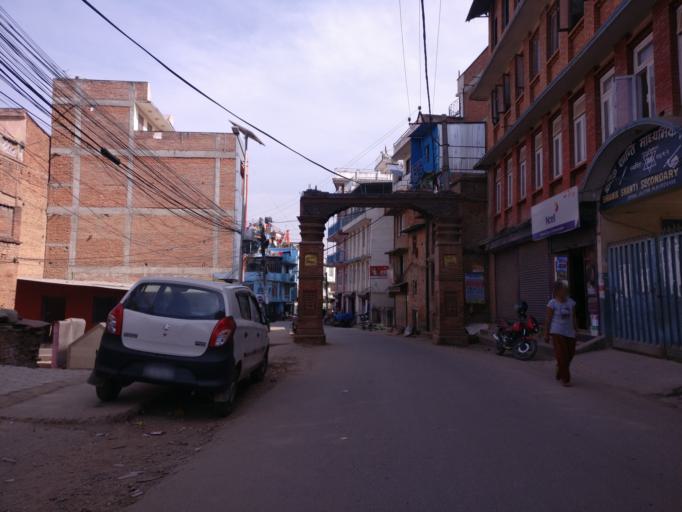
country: NP
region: Central Region
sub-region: Bagmati Zone
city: Patan
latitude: 27.6746
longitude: 85.3289
